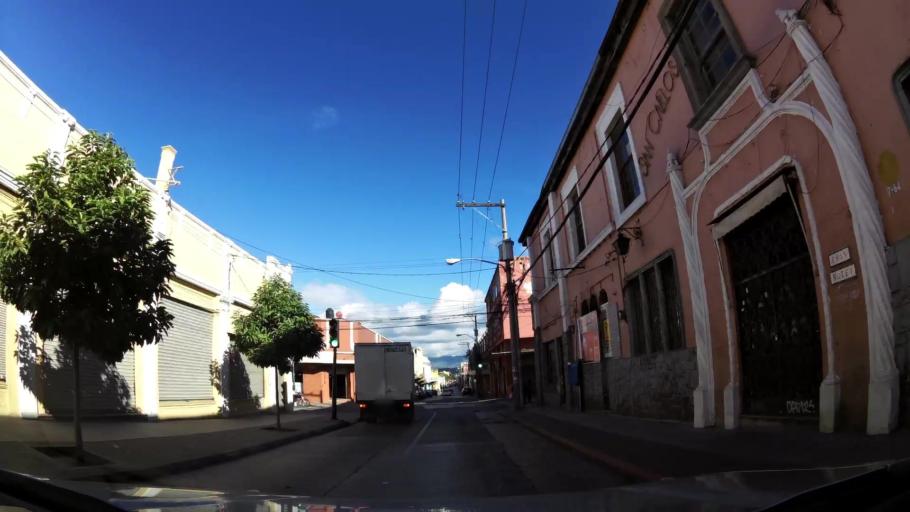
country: GT
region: Guatemala
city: Guatemala City
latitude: 14.6402
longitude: -90.5121
